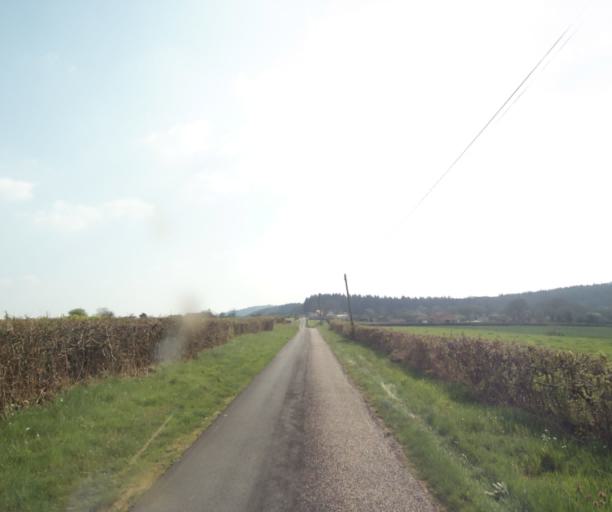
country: FR
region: Bourgogne
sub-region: Departement de Saone-et-Loire
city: Charolles
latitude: 46.4829
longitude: 4.4151
